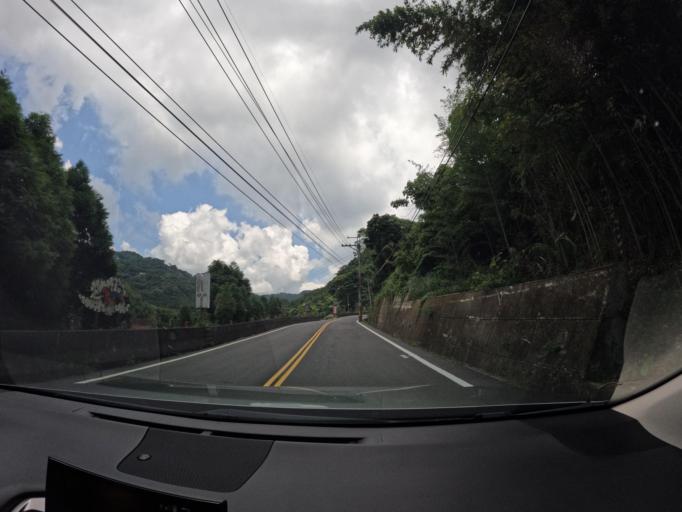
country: TW
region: Taiwan
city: Fengyuan
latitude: 24.3837
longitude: 120.8010
